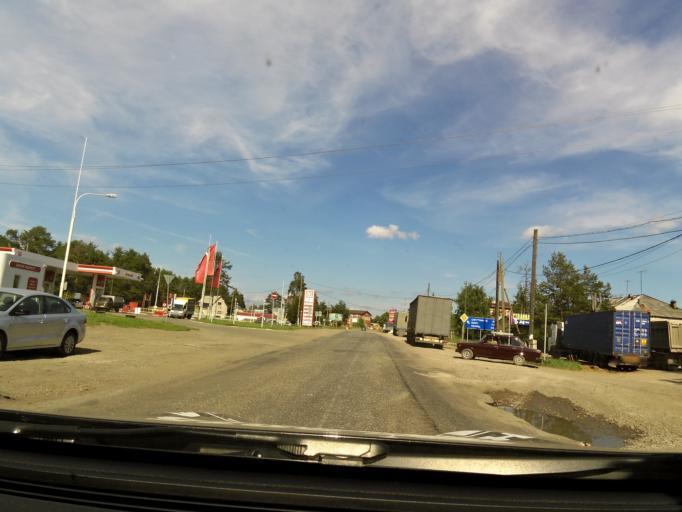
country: RU
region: Kirov
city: Belaya Kholunitsa
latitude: 58.8476
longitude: 50.8239
